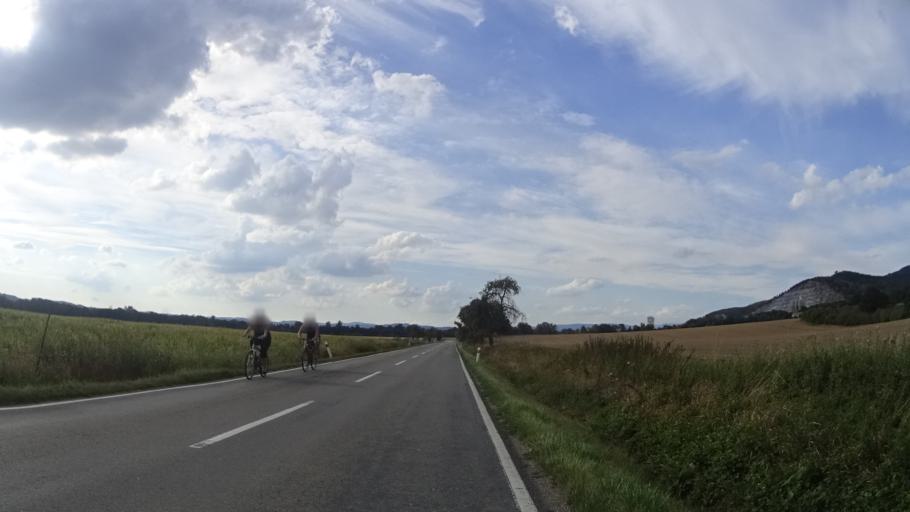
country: CZ
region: Olomoucky
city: Dubicko
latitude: 49.8486
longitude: 16.9471
